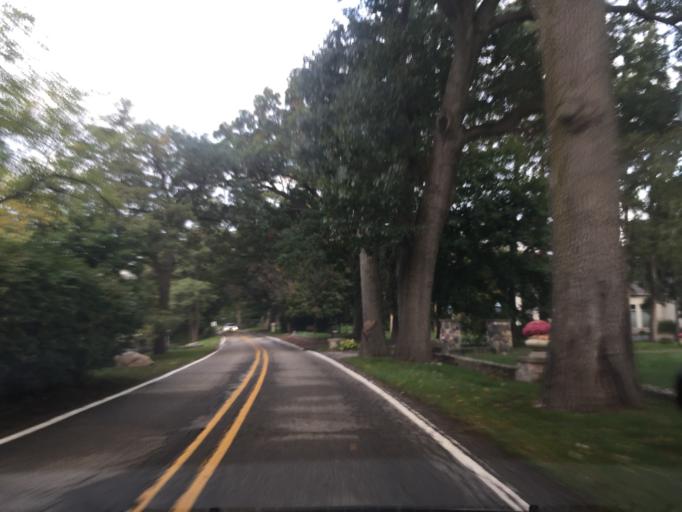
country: US
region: Michigan
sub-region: Oakland County
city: Keego Harbor
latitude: 42.5963
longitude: -83.3367
